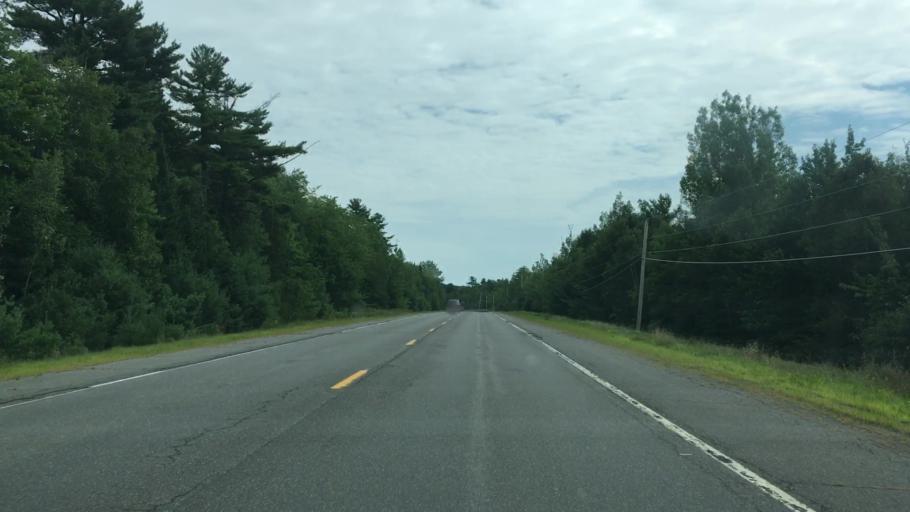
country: US
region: Maine
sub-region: Washington County
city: Calais
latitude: 45.1128
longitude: -67.4172
